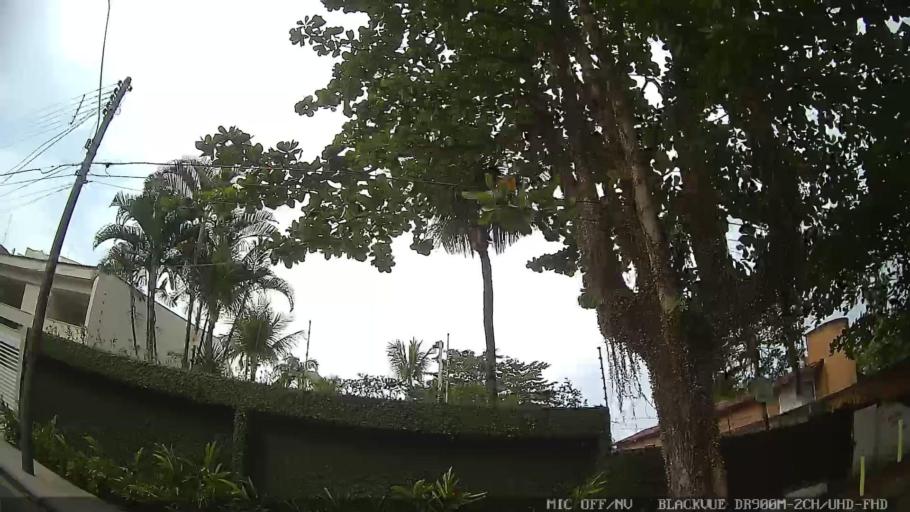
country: BR
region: Sao Paulo
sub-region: Guaruja
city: Guaruja
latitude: -23.9833
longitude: -46.2238
